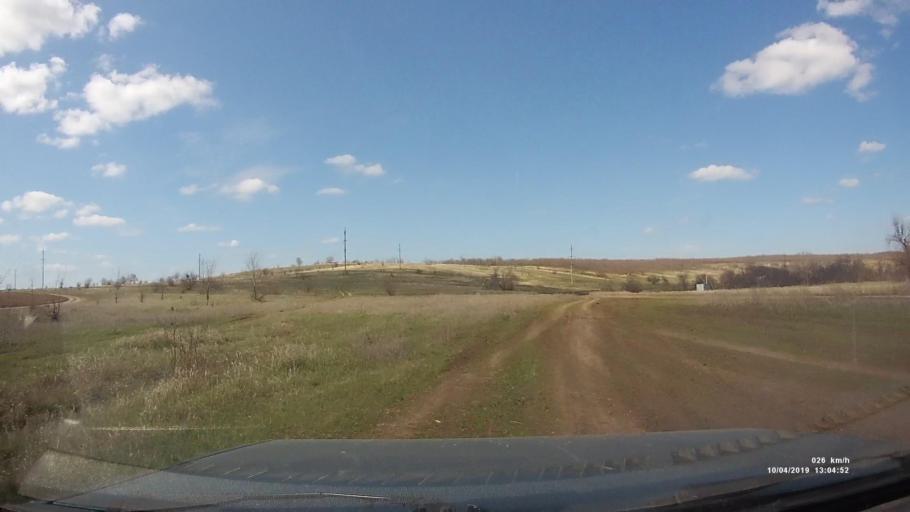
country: RU
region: Rostov
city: Masalovka
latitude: 48.3859
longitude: 40.2348
